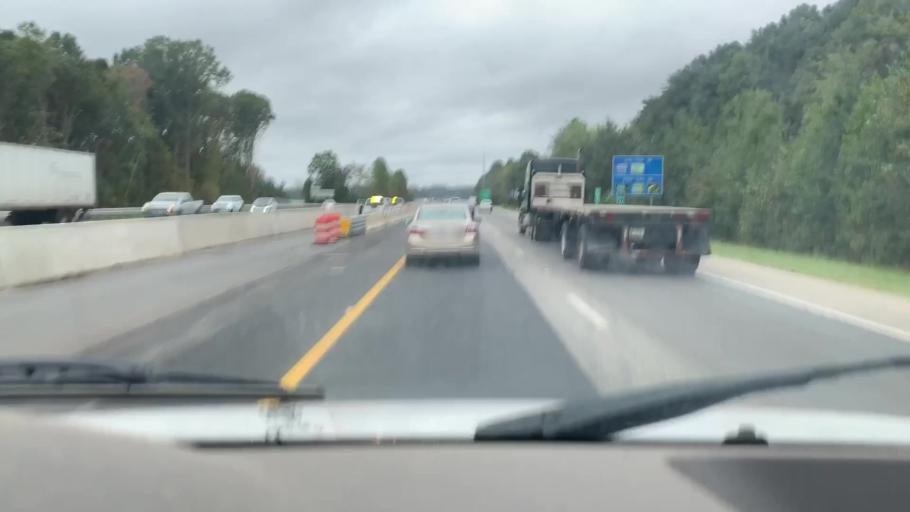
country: US
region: North Carolina
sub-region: Gaston County
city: Davidson
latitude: 35.5230
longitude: -80.8641
